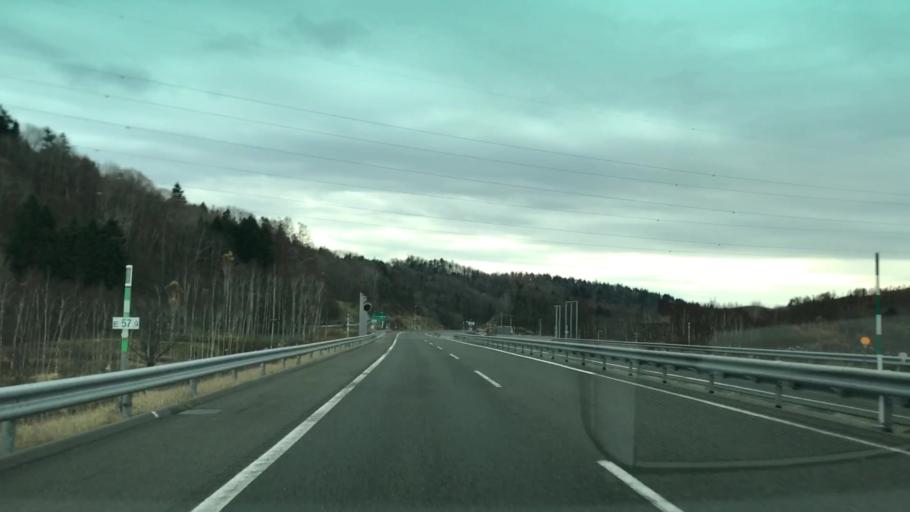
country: JP
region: Hokkaido
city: Shimo-furano
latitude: 42.9297
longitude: 142.2043
